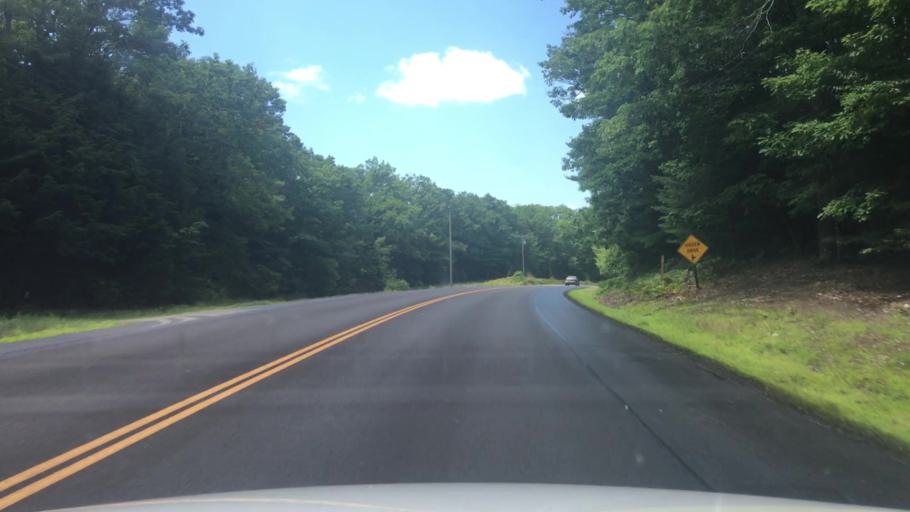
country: US
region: Maine
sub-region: Waldo County
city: Searsmont
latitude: 44.4063
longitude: -69.1958
